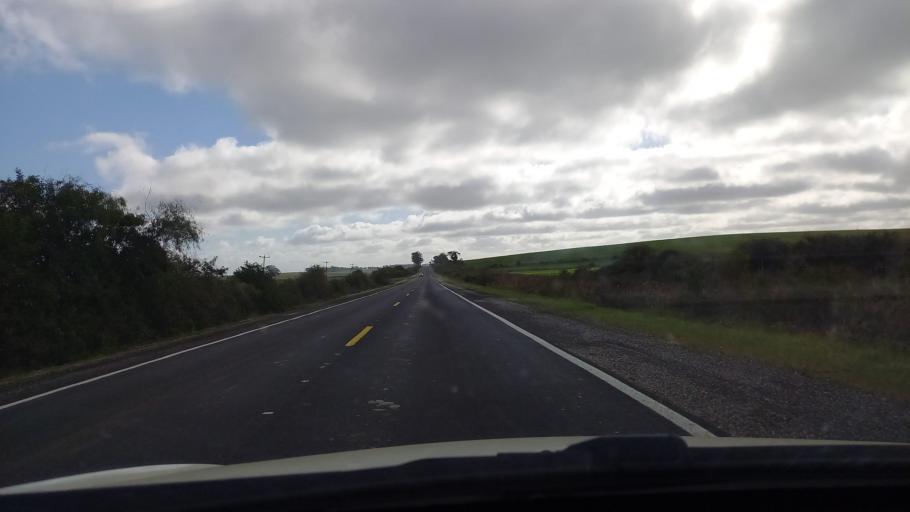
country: BR
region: Rio Grande do Sul
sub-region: Dom Pedrito
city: Dom Pedrito
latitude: -30.8968
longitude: -54.8449
